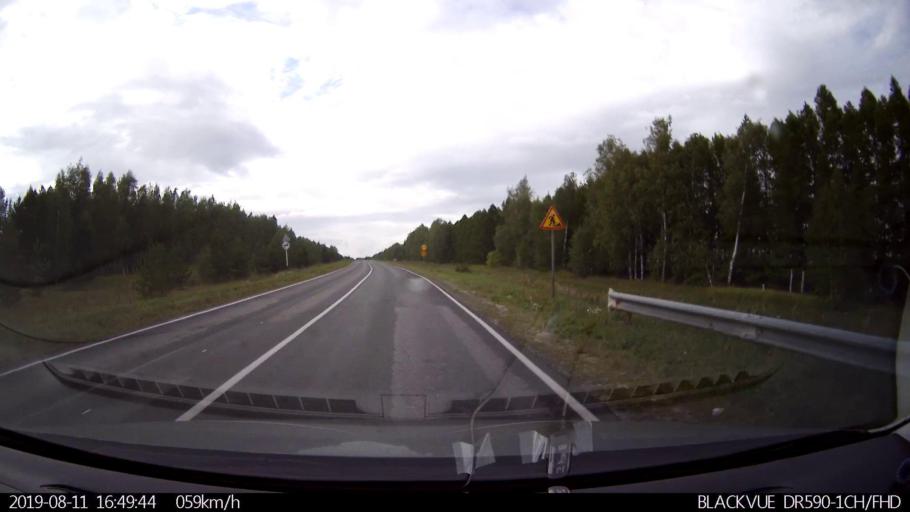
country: RU
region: Ulyanovsk
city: Mayna
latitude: 54.2230
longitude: 47.6950
